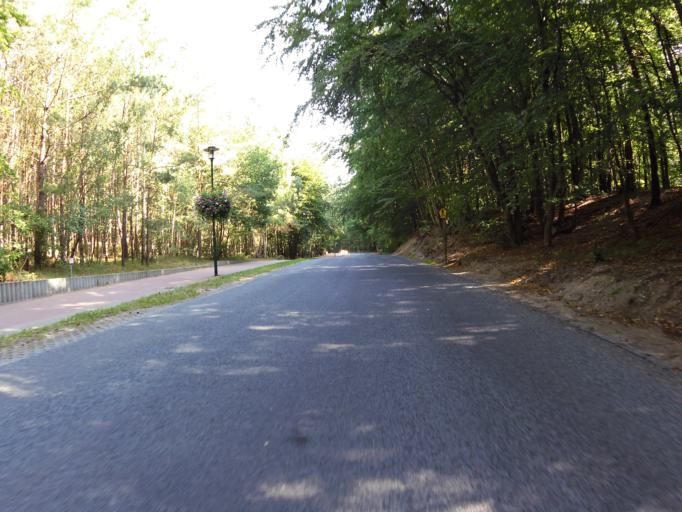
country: DE
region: Mecklenburg-Vorpommern
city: Loddin
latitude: 54.0136
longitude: 14.0570
